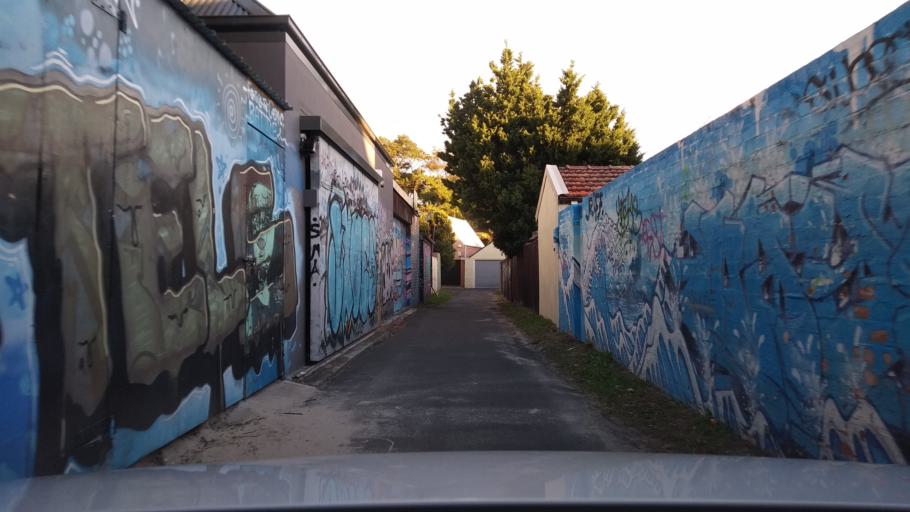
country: AU
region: New South Wales
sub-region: Waverley
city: North Bondi
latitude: -33.8830
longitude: 151.2719
